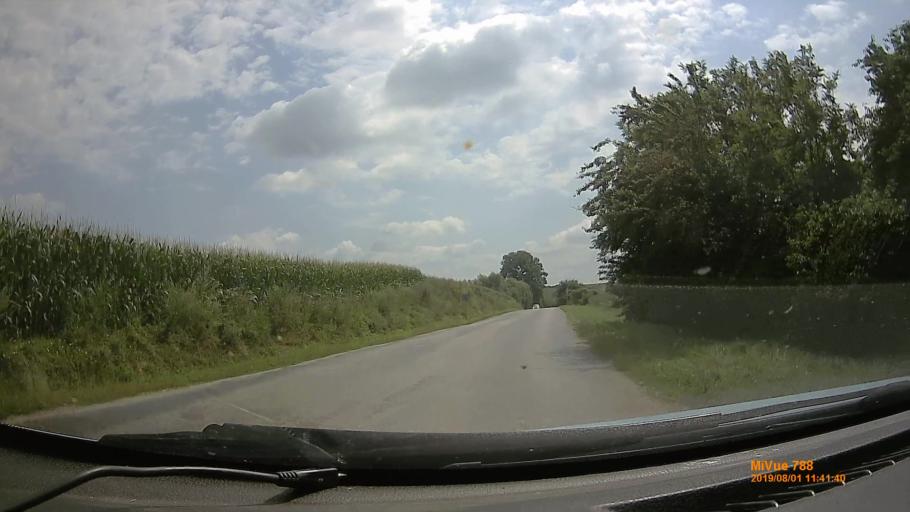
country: HU
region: Baranya
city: Villany
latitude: 45.8903
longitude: 18.4068
